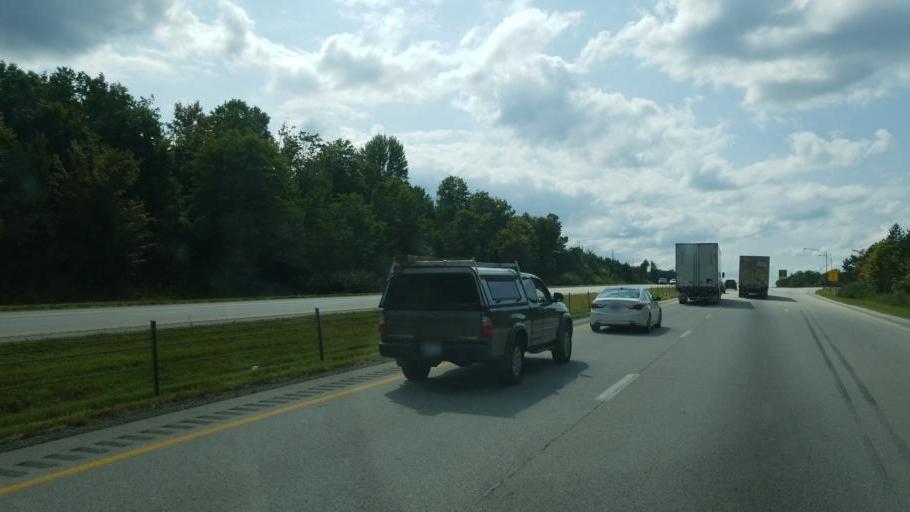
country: US
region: Ohio
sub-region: Wayne County
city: Rittman
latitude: 41.0319
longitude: -81.7966
